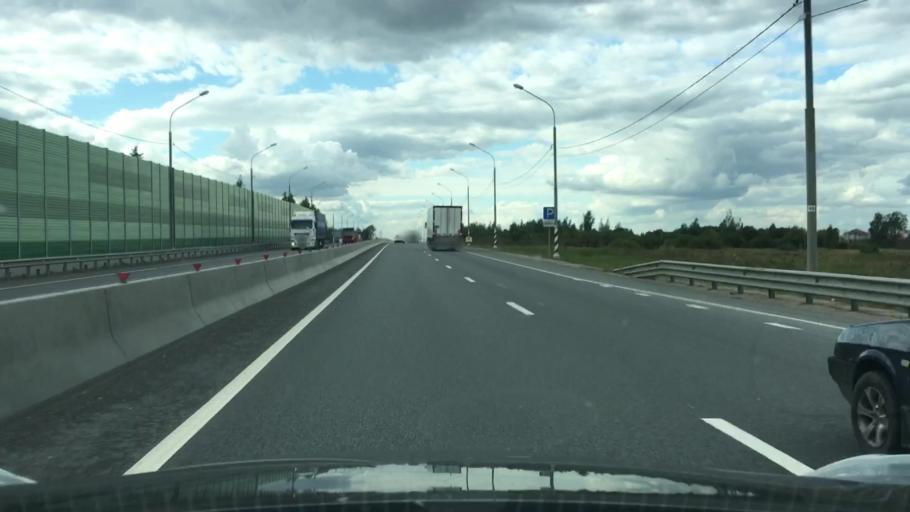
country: RU
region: Tverskaya
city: Tver
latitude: 56.7838
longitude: 35.9389
